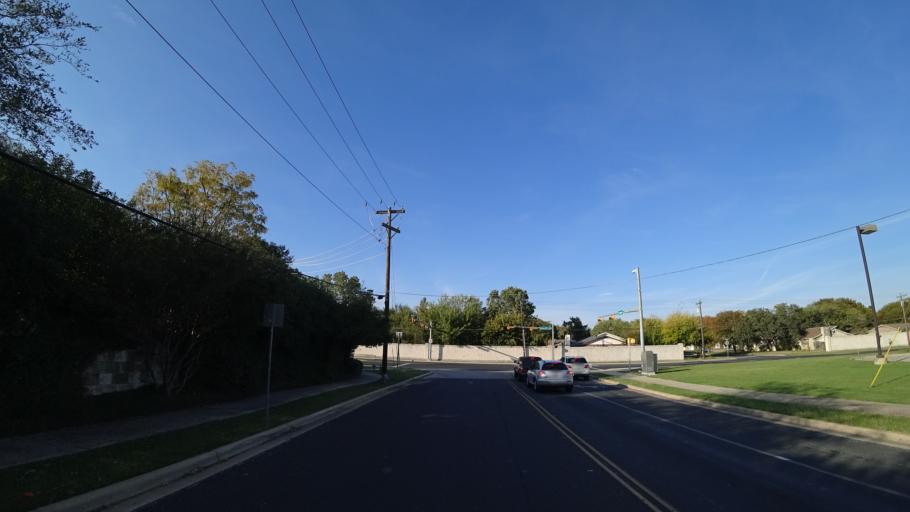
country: US
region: Texas
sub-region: Williamson County
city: Anderson Mill
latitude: 30.4466
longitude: -97.8073
